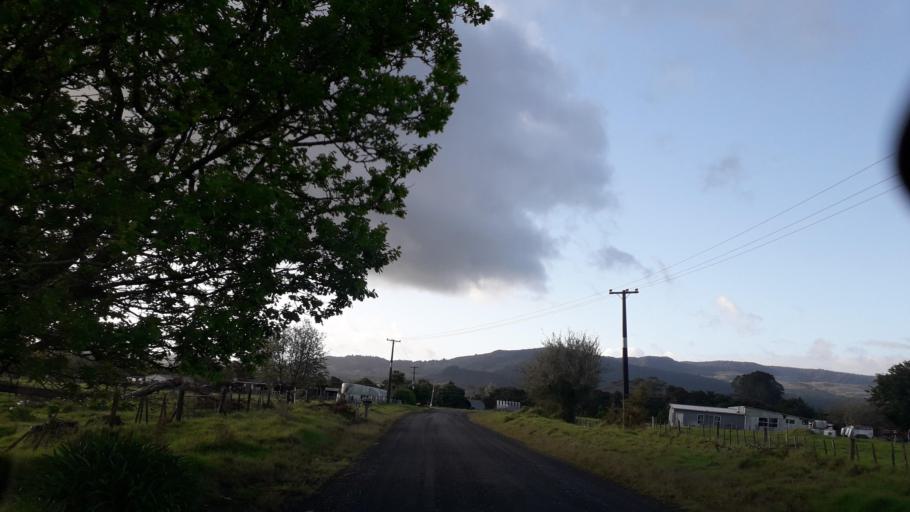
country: NZ
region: Northland
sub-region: Far North District
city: Waimate North
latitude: -35.5011
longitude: 173.6987
